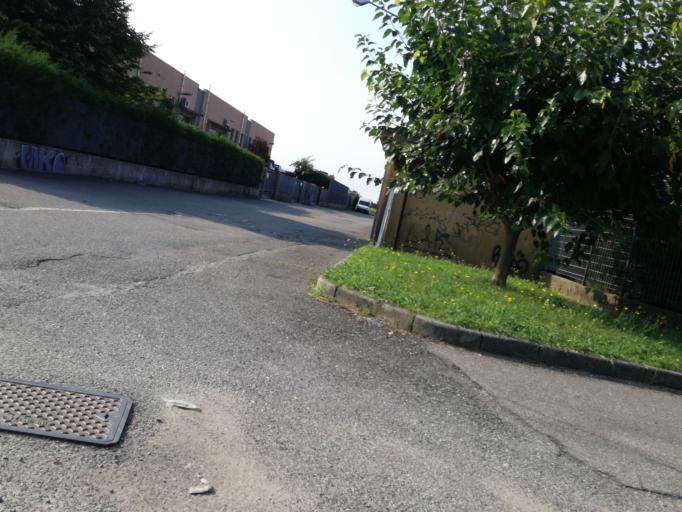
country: IT
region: Lombardy
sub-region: Provincia di Lecco
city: Robbiate
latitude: 45.6783
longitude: 9.4329
